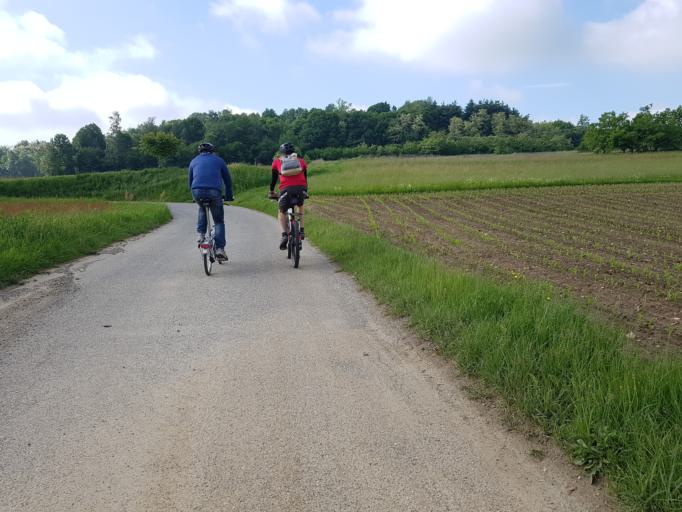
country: IT
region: Piedmont
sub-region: Provincia di Torino
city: San Martino Canavese
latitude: 45.3898
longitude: 7.8186
